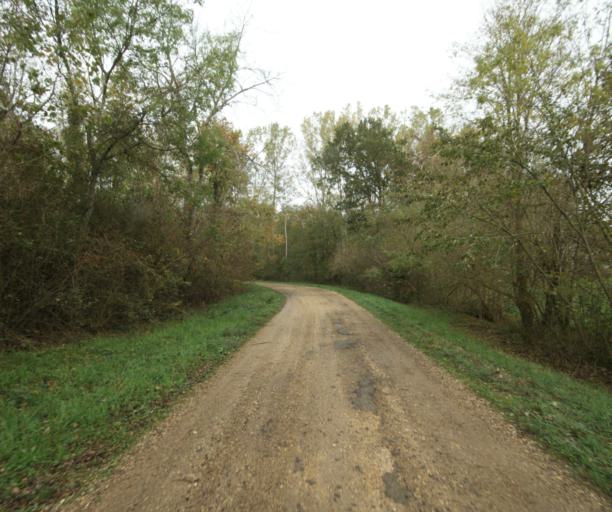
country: FR
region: Rhone-Alpes
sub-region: Departement de l'Ain
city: Pont-de-Vaux
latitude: 46.4624
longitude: 4.9060
